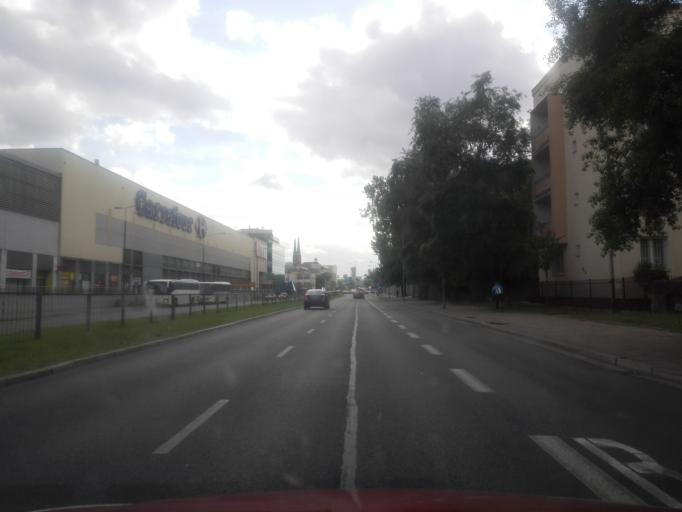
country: PL
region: Masovian Voivodeship
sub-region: Warszawa
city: Praga Polnoc
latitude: 52.2566
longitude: 21.0389
